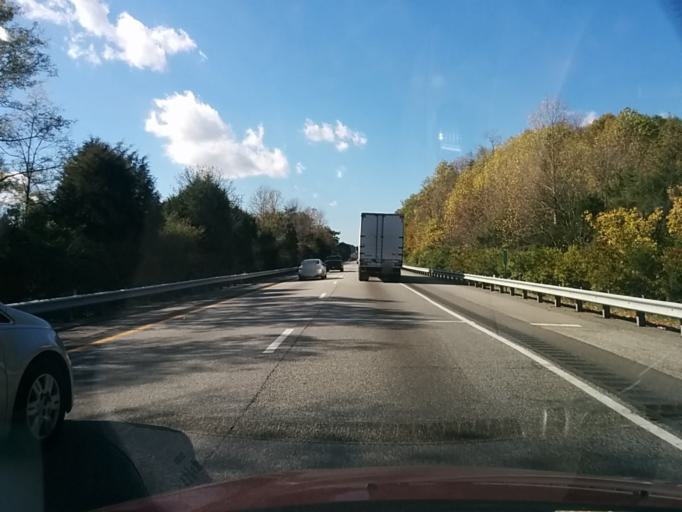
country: US
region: Virginia
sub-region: Botetourt County
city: Fincastle
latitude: 37.4534
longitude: -79.8475
